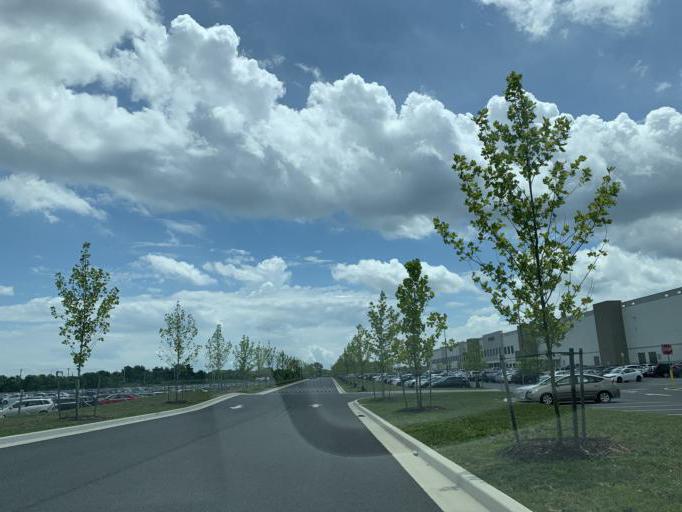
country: US
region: Maryland
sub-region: Baltimore County
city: Edgemere
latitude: 39.2325
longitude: -76.4686
